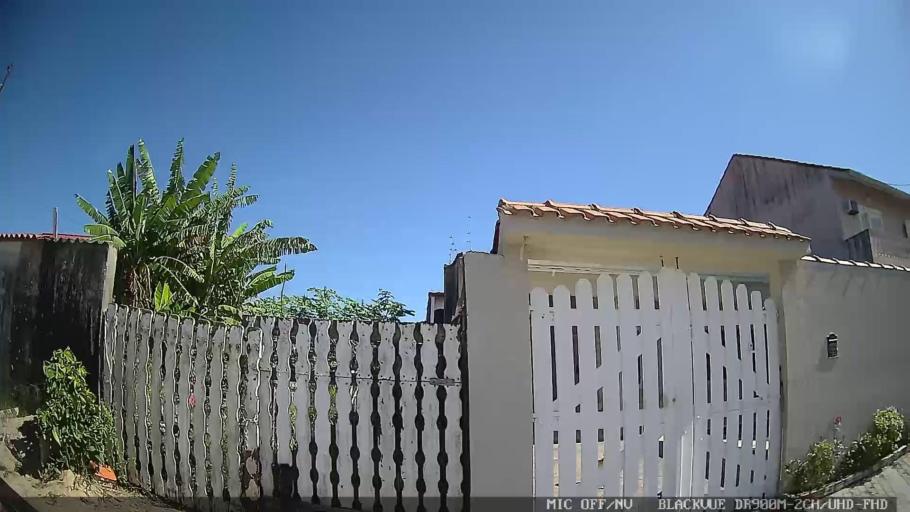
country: BR
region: Sao Paulo
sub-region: Peruibe
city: Peruibe
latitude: -24.2774
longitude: -46.9424
